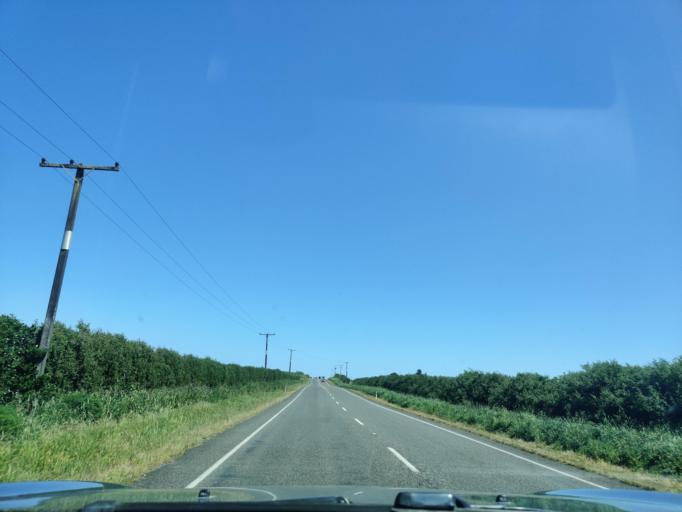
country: NZ
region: Taranaki
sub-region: South Taranaki District
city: Patea
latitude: -39.7468
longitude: 174.5053
